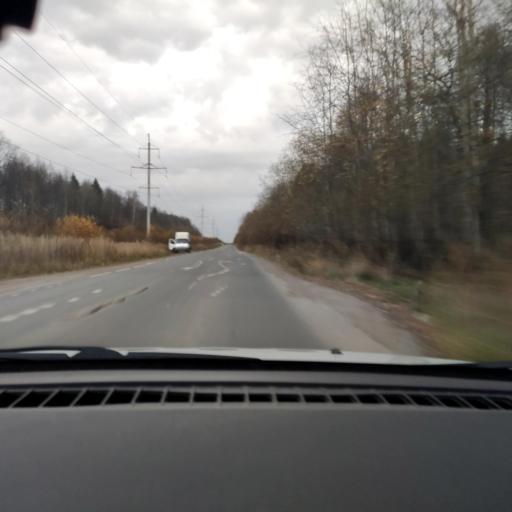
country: RU
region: Perm
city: Perm
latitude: 58.0942
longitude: 56.4042
